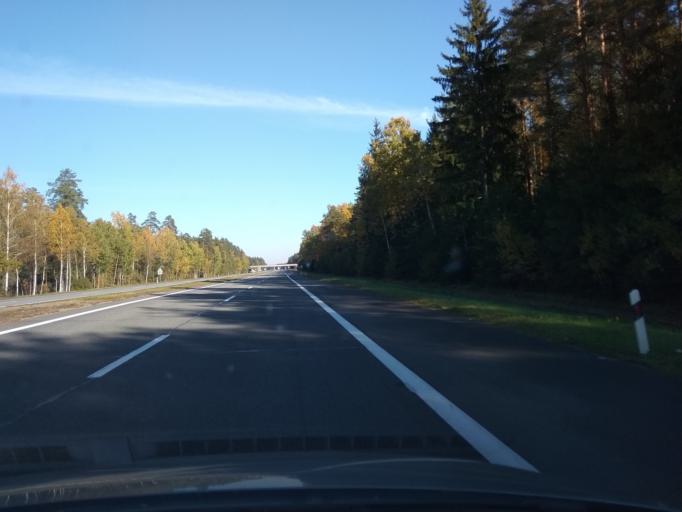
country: BY
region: Brest
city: Baranovichi
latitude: 53.0442
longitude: 25.8349
